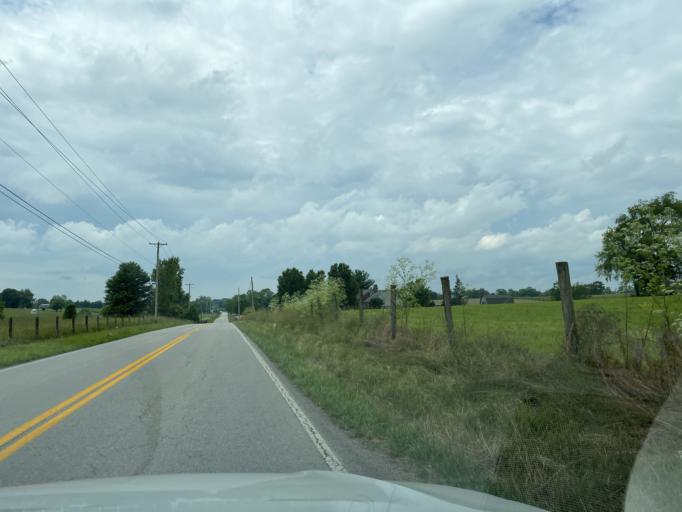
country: US
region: Kentucky
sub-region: Scott County
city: Georgetown
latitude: 38.2226
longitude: -84.4494
